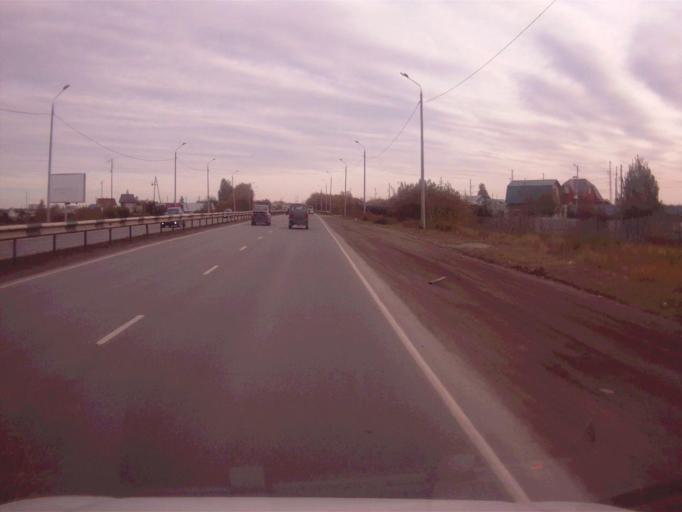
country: RU
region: Chelyabinsk
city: Novosineglazovskiy
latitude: 55.0448
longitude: 61.4214
